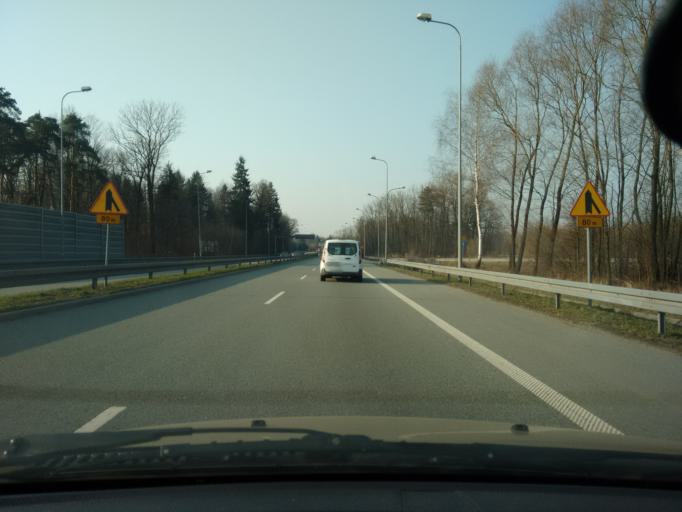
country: PL
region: Silesian Voivodeship
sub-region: Powiat cieszynski
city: Skoczow
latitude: 49.7864
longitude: 18.8036
